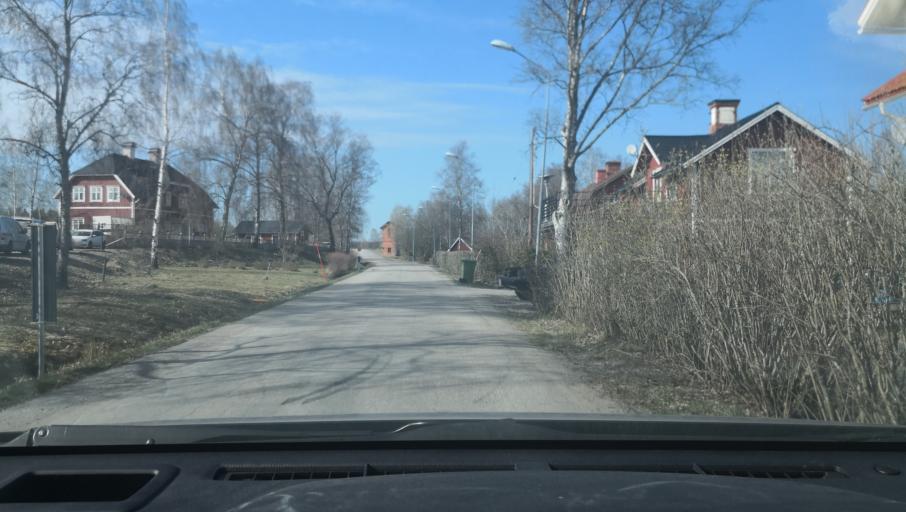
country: SE
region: Uppsala
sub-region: Heby Kommun
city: Morgongava
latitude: 59.8417
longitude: 16.9161
